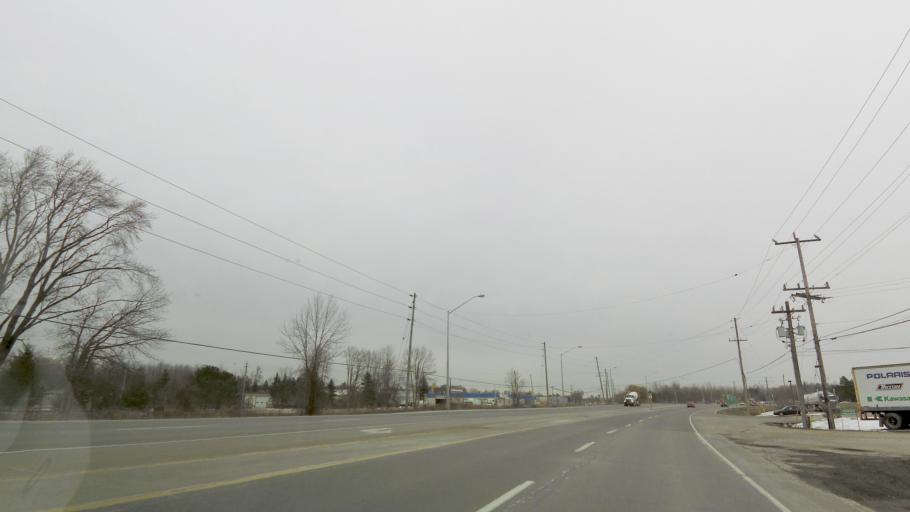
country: CA
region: Ontario
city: Newmarket
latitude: 44.1069
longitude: -79.5227
